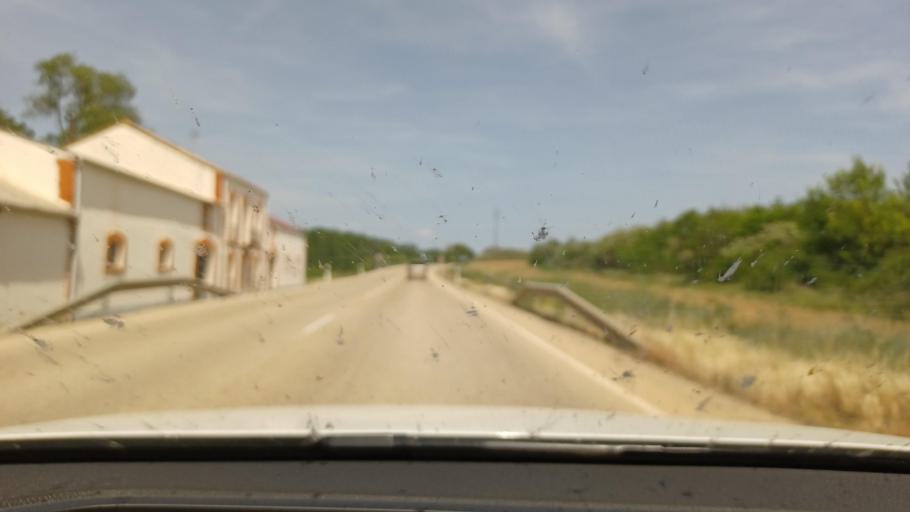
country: ES
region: Castille and Leon
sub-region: Provincia de Soria
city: Almazan
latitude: 41.4738
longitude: -2.5603
